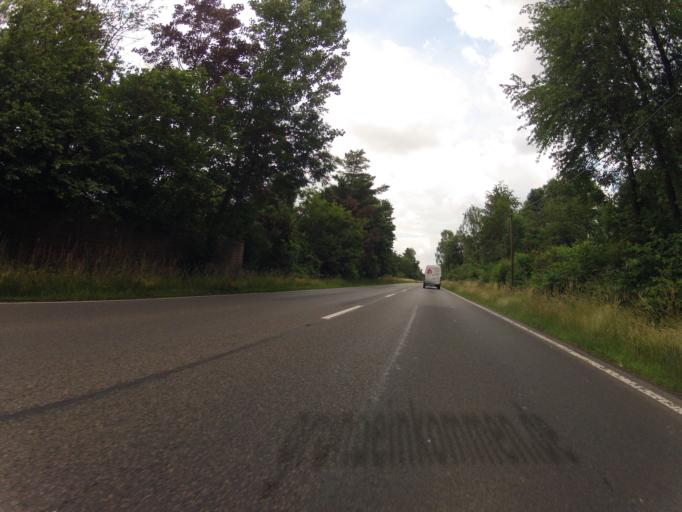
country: DE
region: Saxony
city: Machern
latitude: 51.3583
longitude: 12.6348
